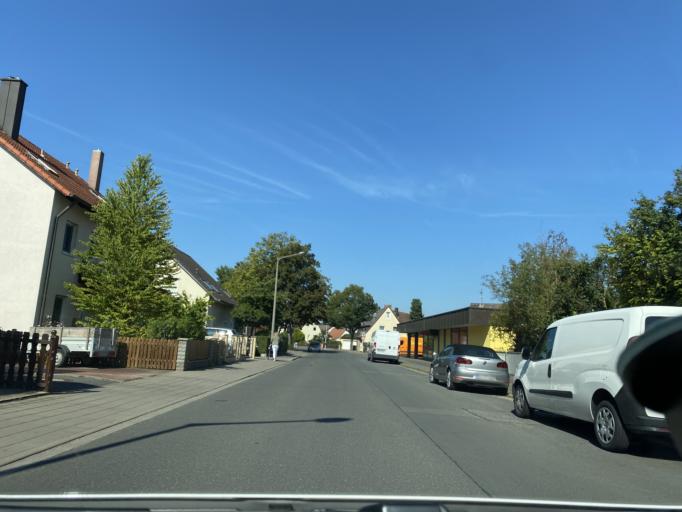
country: DE
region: Bavaria
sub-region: Regierungsbezirk Mittelfranken
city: Furth
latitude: 49.5012
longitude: 11.0165
